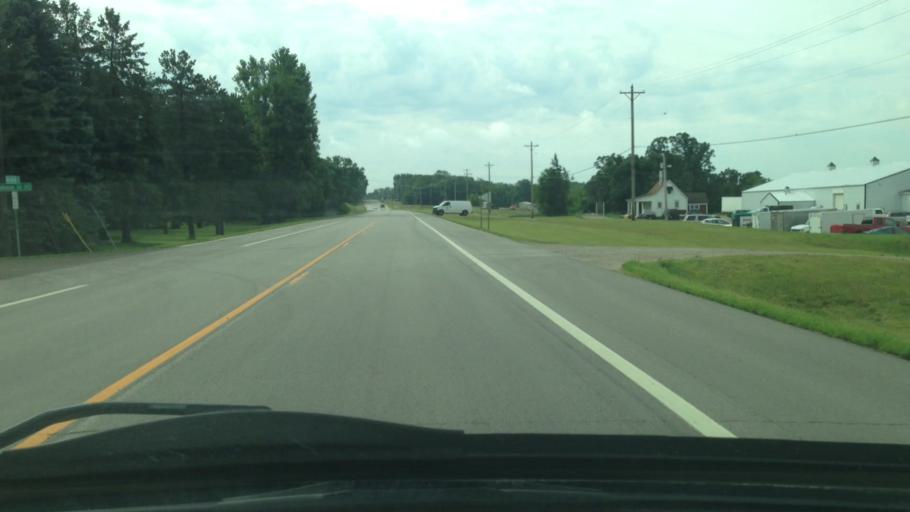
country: US
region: Minnesota
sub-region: Olmsted County
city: Rochester
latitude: 43.9828
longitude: -92.4013
